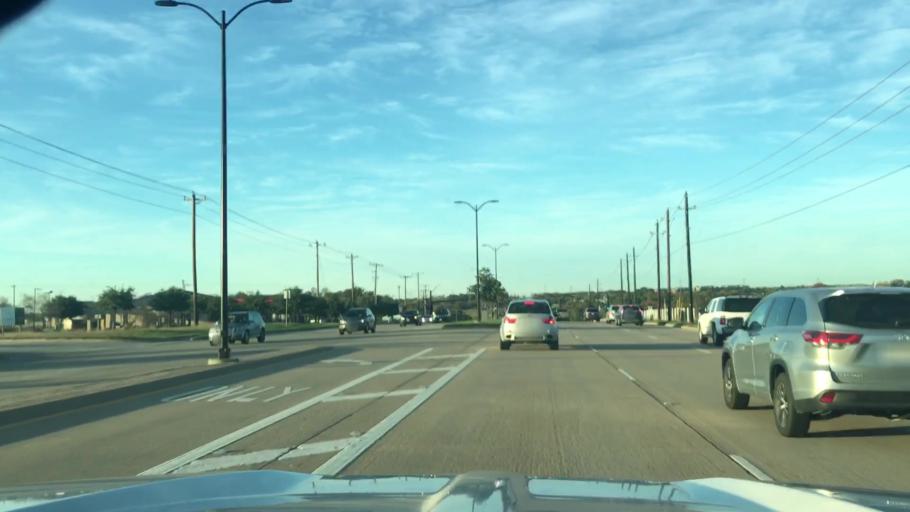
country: US
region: Texas
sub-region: Collin County
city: Frisco
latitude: 33.1722
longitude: -96.8030
